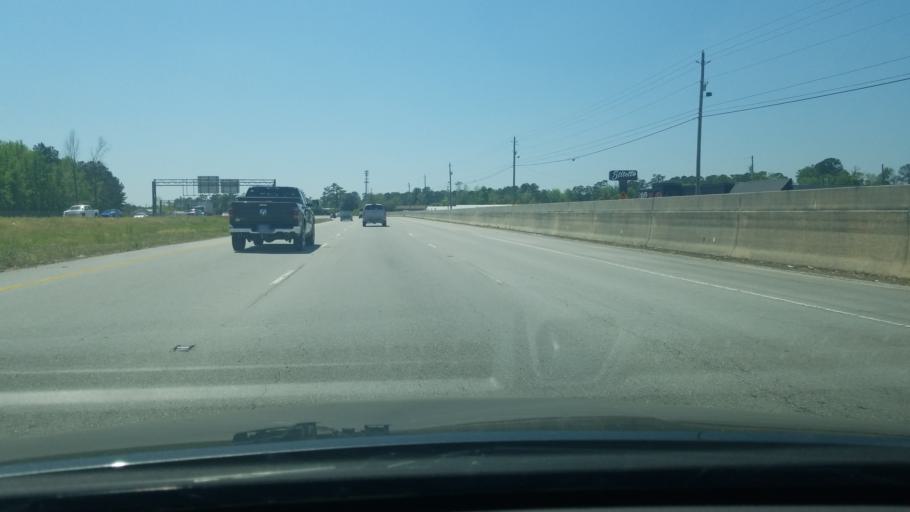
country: US
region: North Carolina
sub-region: Onslow County
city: Jacksonville
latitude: 34.7389
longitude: -77.4642
